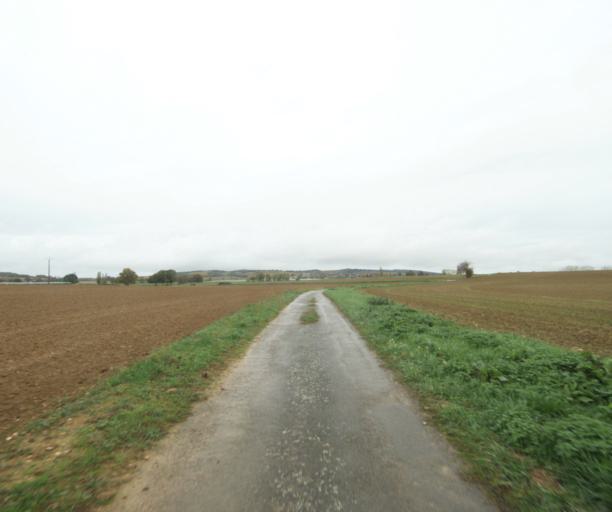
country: FR
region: Rhone-Alpes
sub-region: Departement de l'Ain
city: Pont-de-Vaux
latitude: 46.4859
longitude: 4.8796
